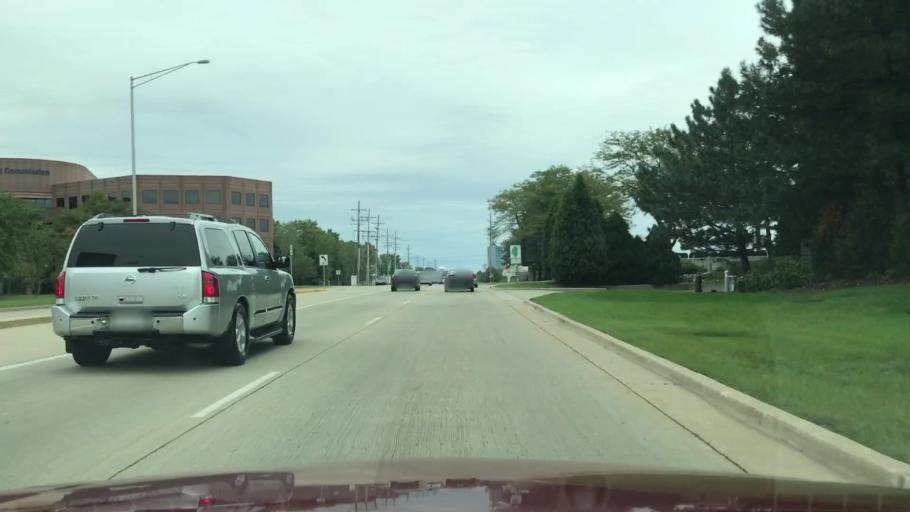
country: US
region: Illinois
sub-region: DuPage County
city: Oakbrook Terrace
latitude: 41.8467
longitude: -87.9823
